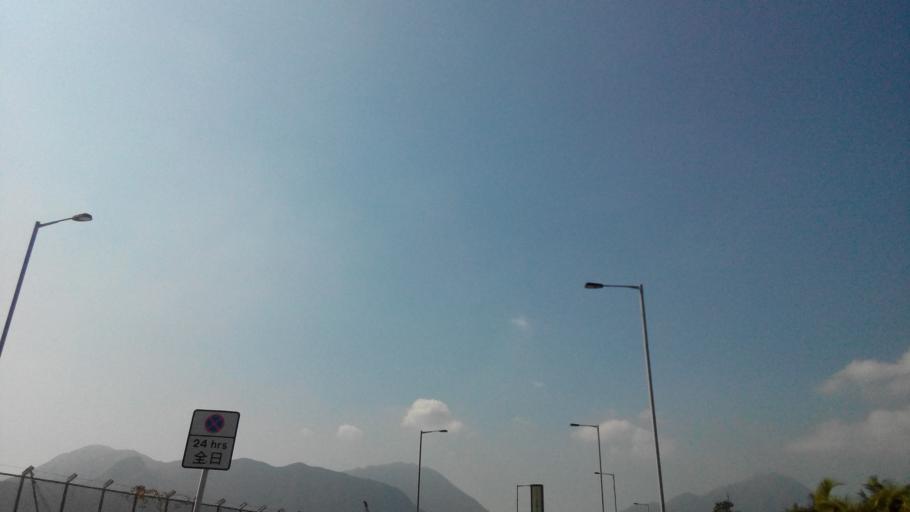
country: HK
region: Tuen Mun
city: Tuen Mun
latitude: 22.3174
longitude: 113.9434
